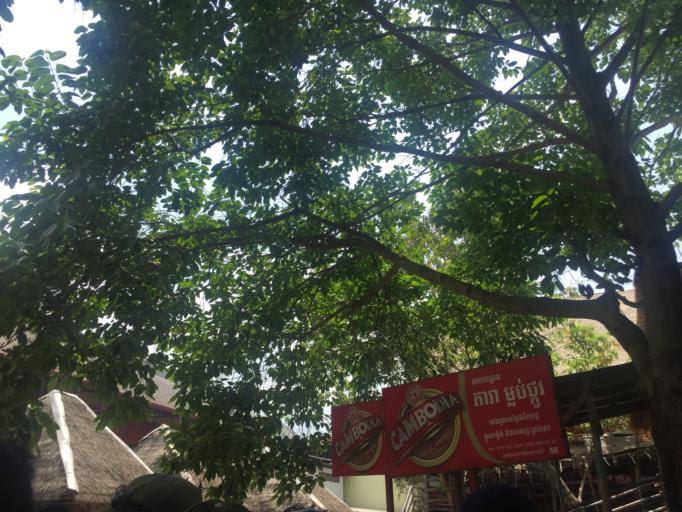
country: KH
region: Kandal
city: Ta Khmau
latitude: 11.5132
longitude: 105.0398
